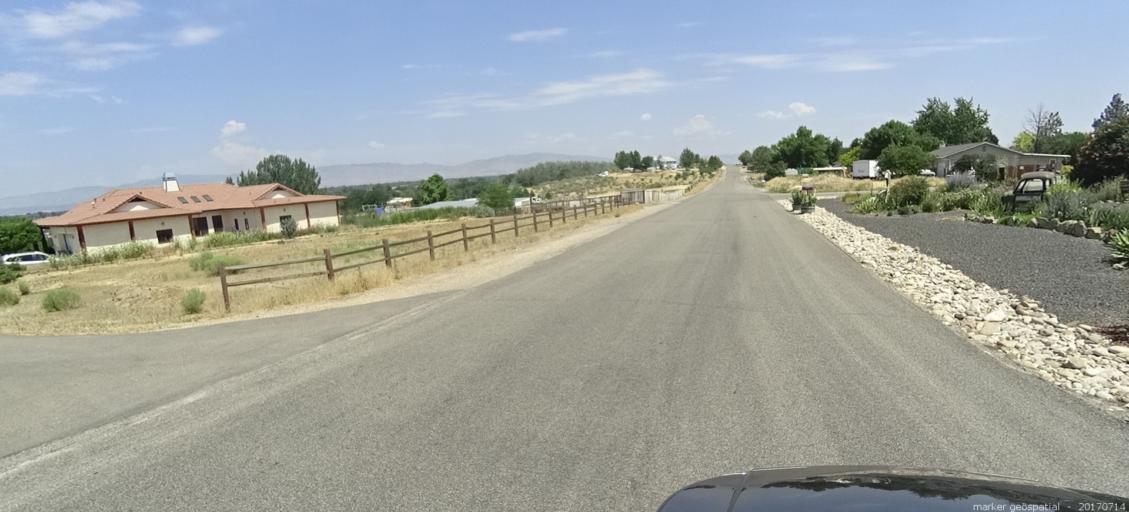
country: US
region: Idaho
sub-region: Ada County
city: Meridian
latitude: 43.5355
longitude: -116.3220
